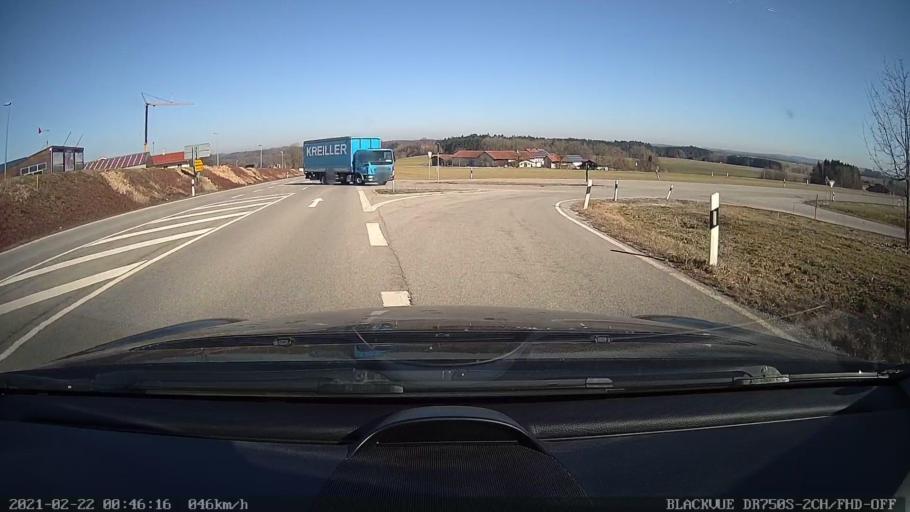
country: DE
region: Bavaria
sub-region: Upper Bavaria
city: Griesstatt
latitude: 48.0007
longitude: 12.1791
